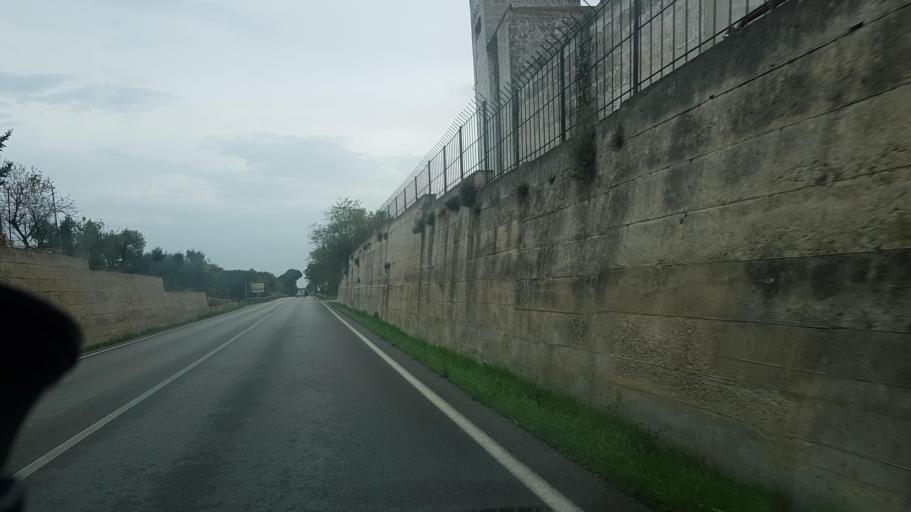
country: IT
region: Apulia
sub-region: Provincia di Brindisi
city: Ostuni
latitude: 40.7180
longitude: 17.6141
